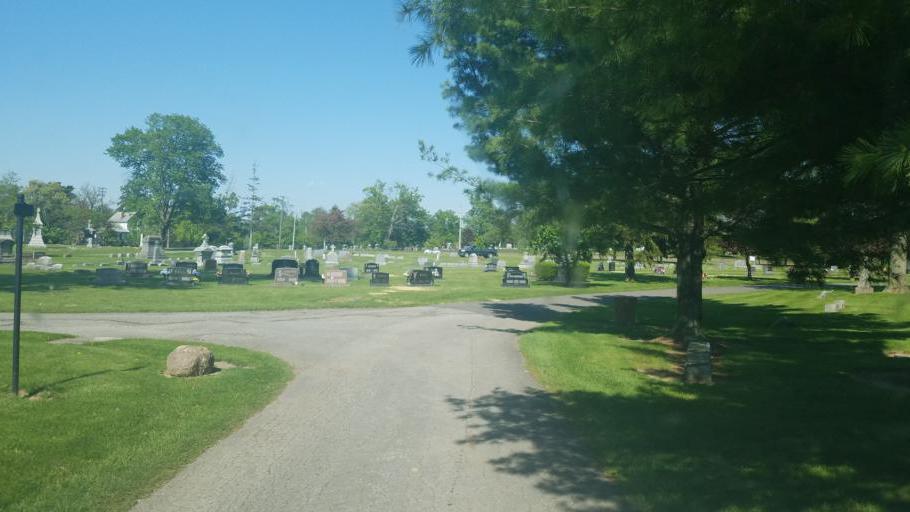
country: US
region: Ohio
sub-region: Marion County
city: Marion
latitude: 40.5750
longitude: -83.1268
